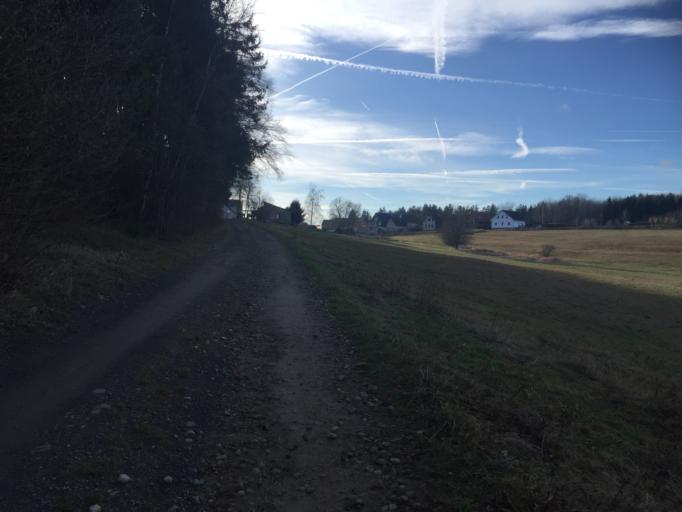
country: DE
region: Thuringia
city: Doschnitz
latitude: 50.6413
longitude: 11.2577
